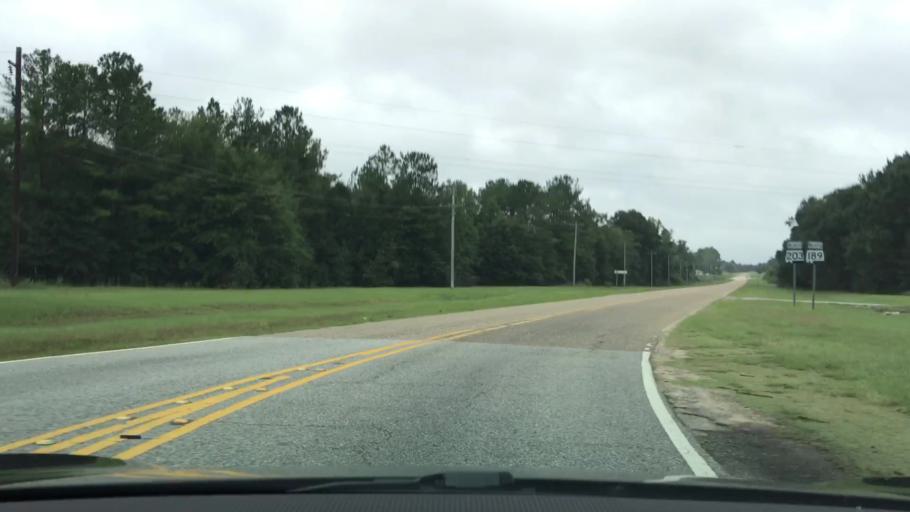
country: US
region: Alabama
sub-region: Coffee County
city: Elba
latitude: 31.4055
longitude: -86.0815
